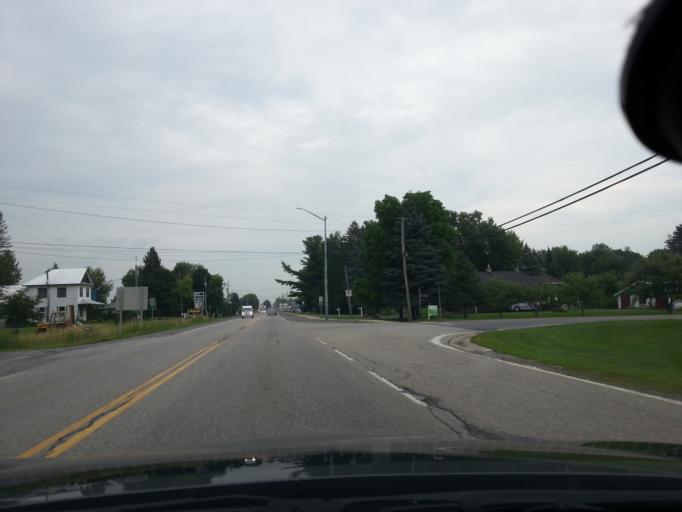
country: CA
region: Quebec
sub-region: Outaouais
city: Papineauville
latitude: 45.5548
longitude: -74.8938
